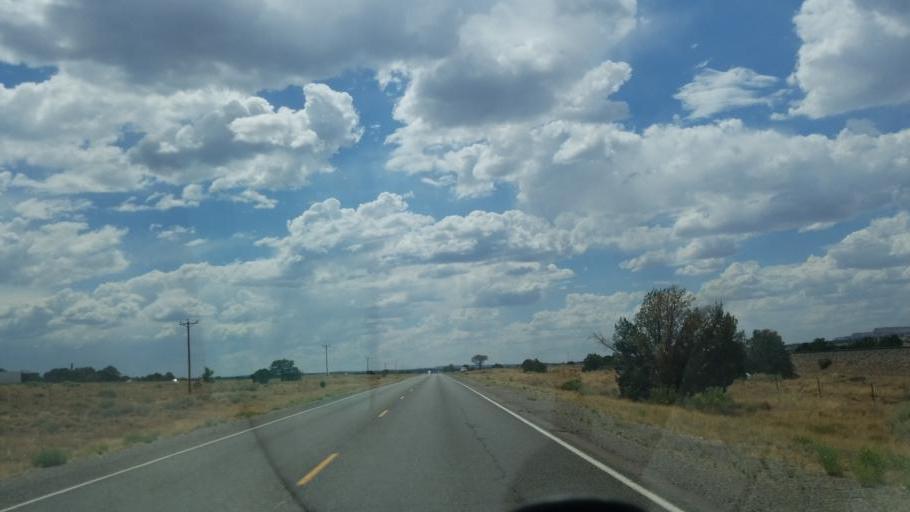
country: US
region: New Mexico
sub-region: McKinley County
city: Thoreau
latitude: 35.3896
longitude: -108.1769
